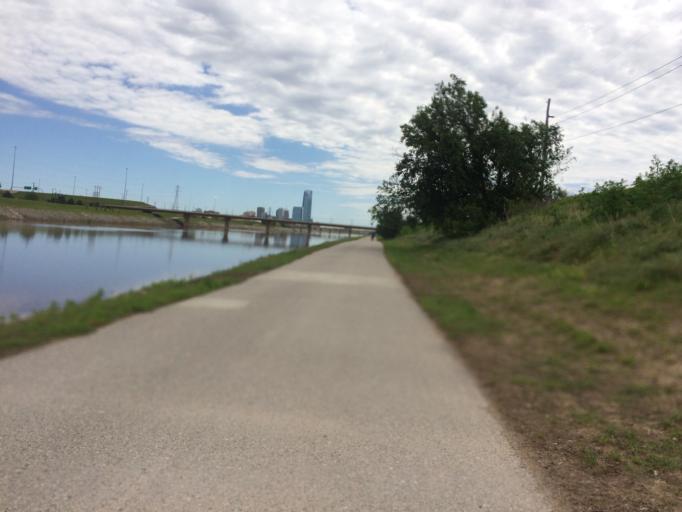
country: US
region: Oklahoma
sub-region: Oklahoma County
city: Oklahoma City
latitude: 35.4580
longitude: -97.5596
